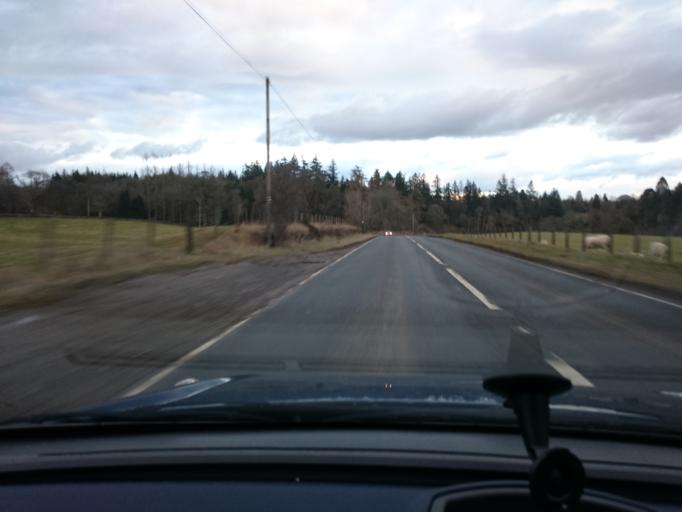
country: GB
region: Scotland
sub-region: Stirling
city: Doune
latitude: 56.2064
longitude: -4.1217
